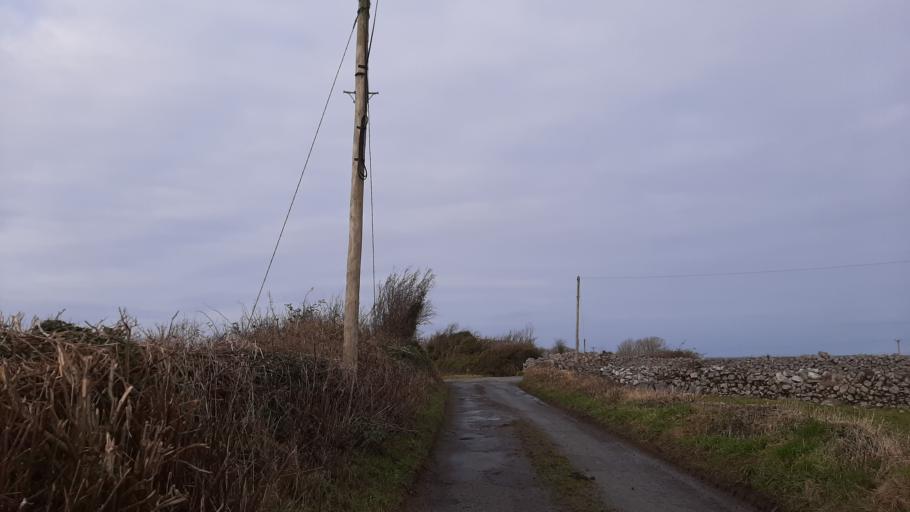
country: IE
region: Connaught
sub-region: County Galway
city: Gaillimh
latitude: 53.3176
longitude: -9.0561
